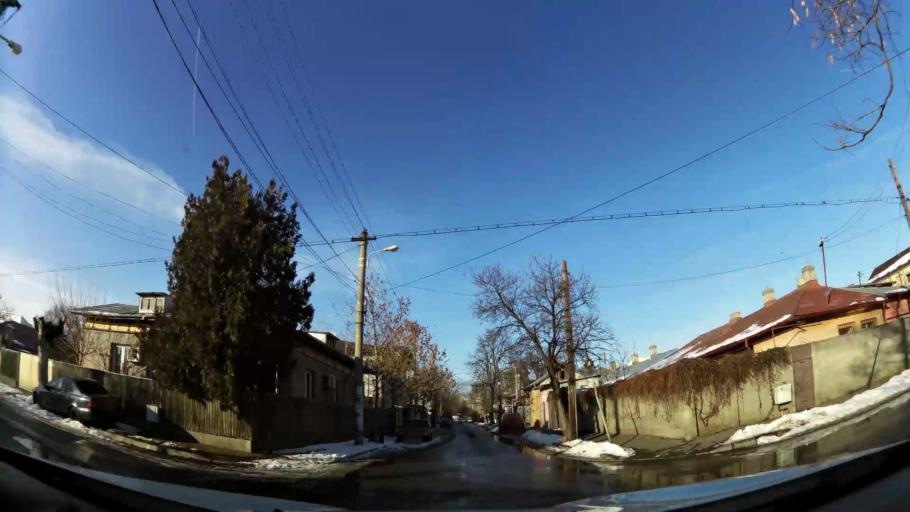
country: RO
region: Bucuresti
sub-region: Municipiul Bucuresti
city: Bucuresti
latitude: 44.3977
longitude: 26.0913
